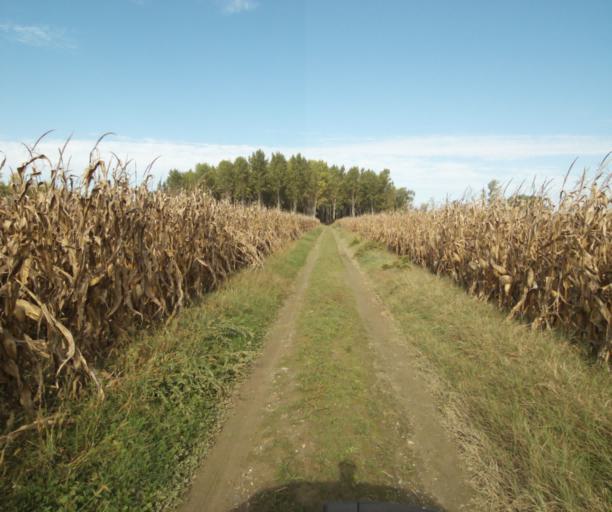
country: FR
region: Midi-Pyrenees
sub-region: Departement du Tarn-et-Garonne
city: Finhan
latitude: 43.9087
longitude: 1.2113
